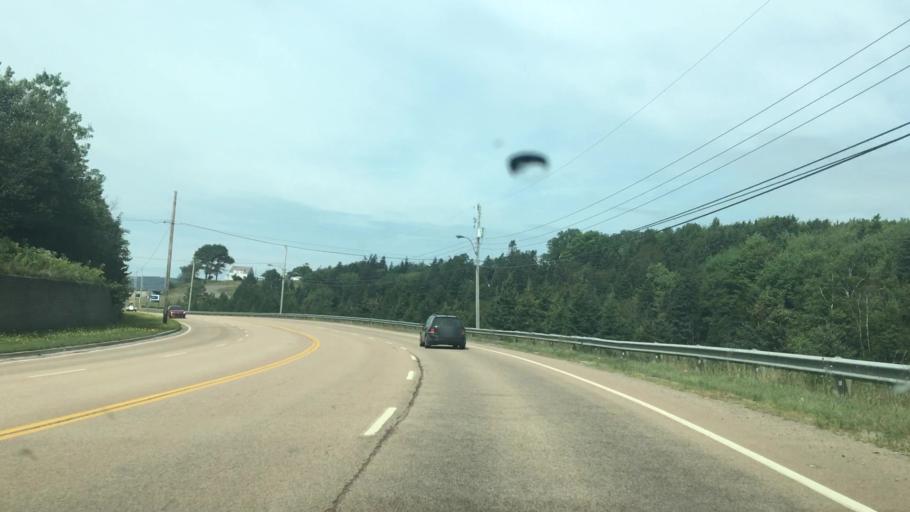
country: CA
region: Nova Scotia
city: Port Hawkesbury
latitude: 45.6247
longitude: -61.3660
